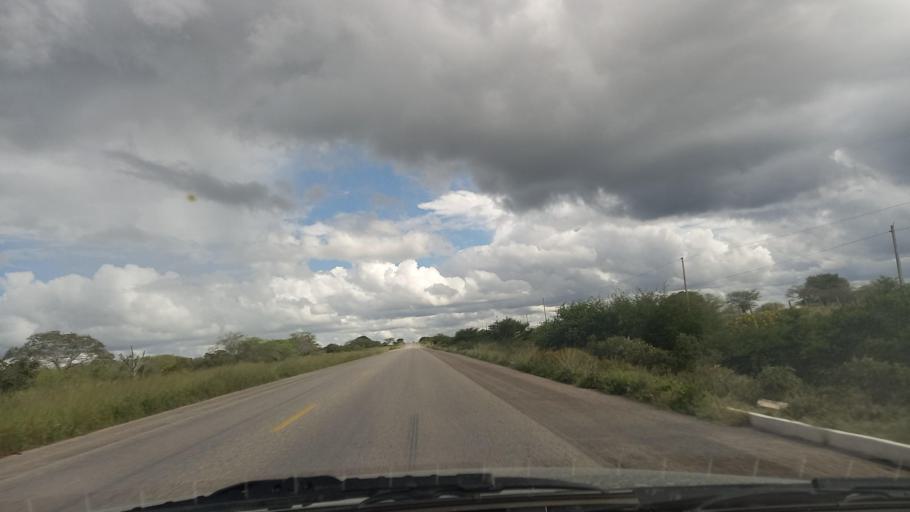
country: BR
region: Pernambuco
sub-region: Cachoeirinha
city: Cachoeirinha
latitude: -8.5159
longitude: -36.2553
